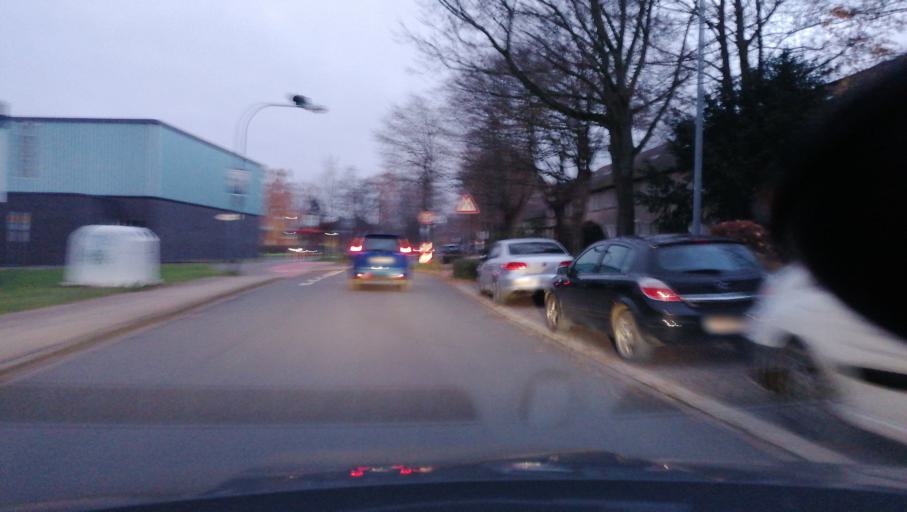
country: DE
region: North Rhine-Westphalia
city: Herten
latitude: 51.6014
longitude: 7.1246
